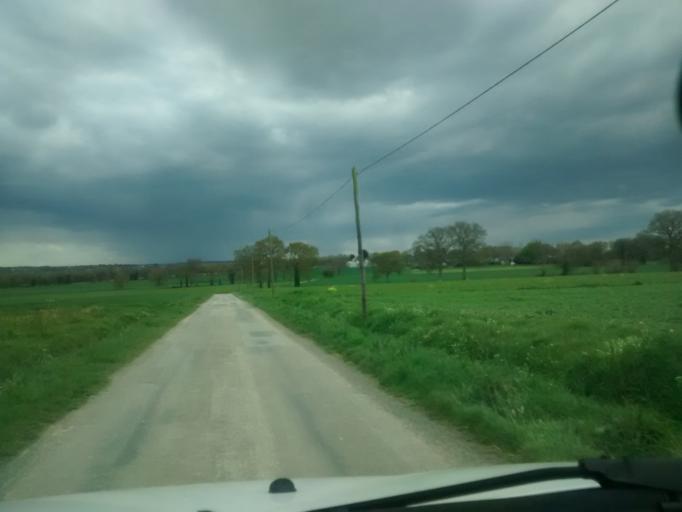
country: FR
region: Brittany
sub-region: Departement d'Ille-et-Vilaine
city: Servon-sur-Vilaine
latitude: 48.1506
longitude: -1.4913
